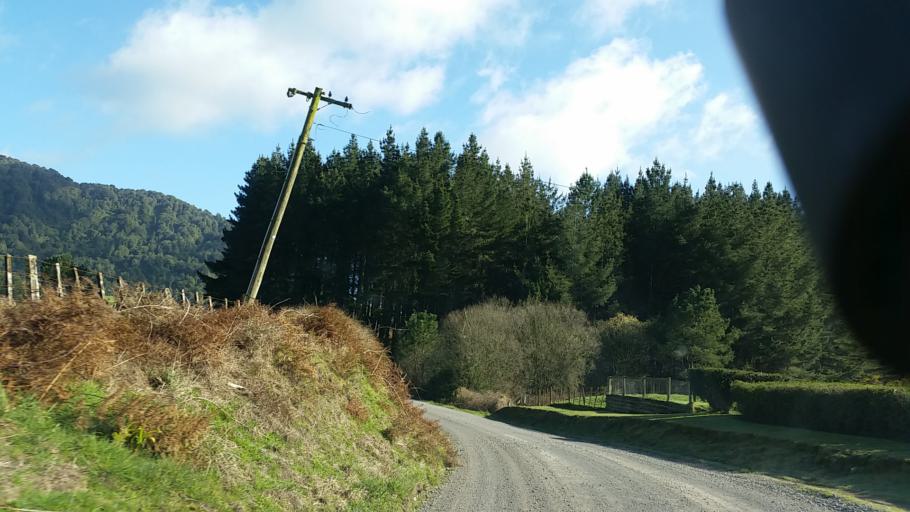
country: NZ
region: Bay of Plenty
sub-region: Rotorua District
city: Rotorua
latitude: -38.2365
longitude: 176.1690
